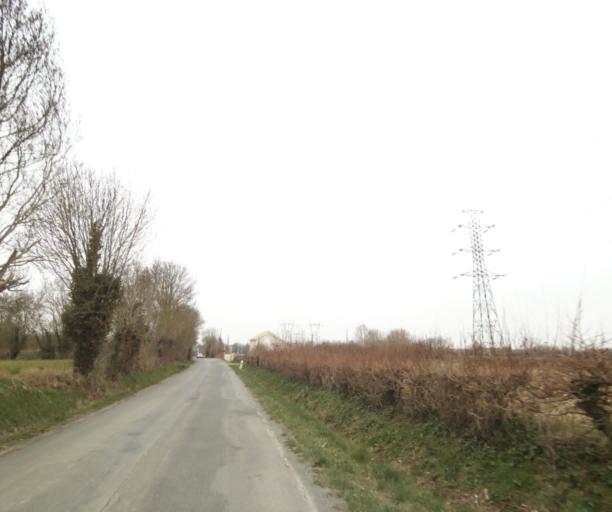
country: FR
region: Poitou-Charentes
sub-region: Departement des Deux-Sevres
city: Niort
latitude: 46.3023
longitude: -0.4778
